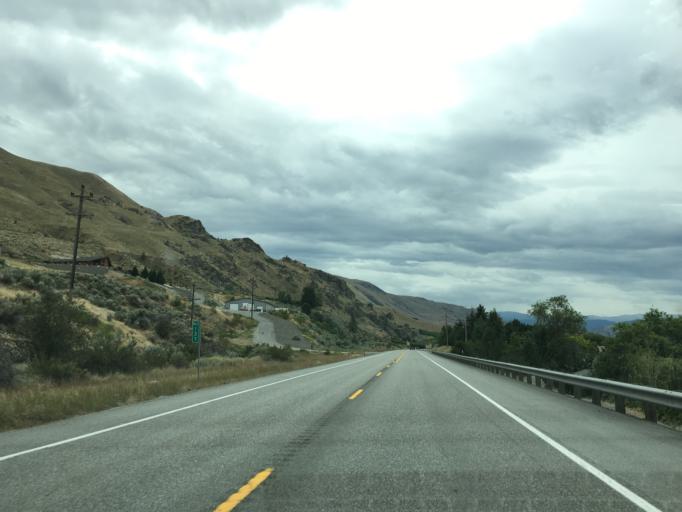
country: US
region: Washington
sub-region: Chelan County
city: Entiat
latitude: 47.5840
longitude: -120.2351
